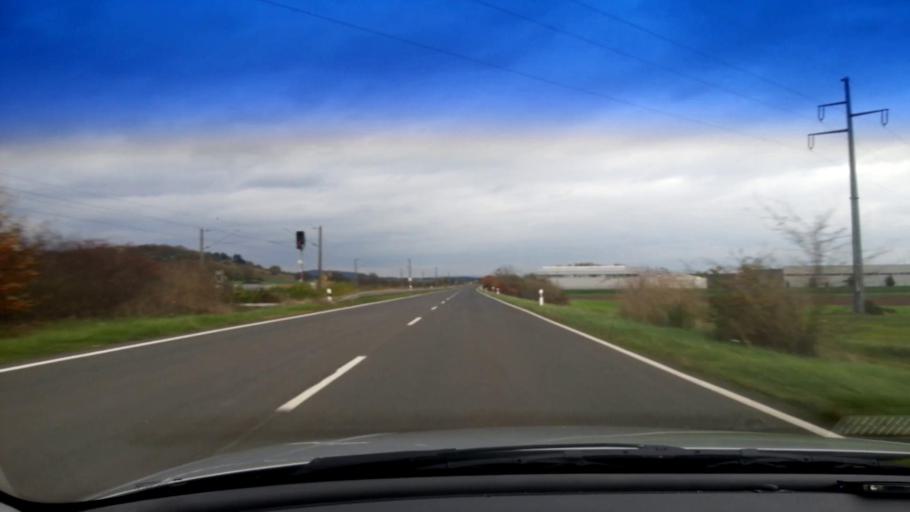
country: DE
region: Bavaria
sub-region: Upper Franconia
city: Viereth-Trunstadt
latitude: 49.9390
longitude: 10.7752
